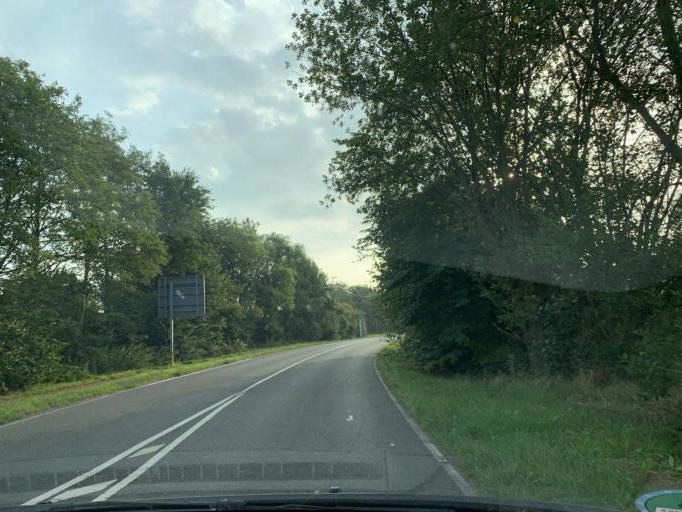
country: DE
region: North Rhine-Westphalia
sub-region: Regierungsbezirk Koln
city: Erftstadt
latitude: 50.8000
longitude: 6.8190
